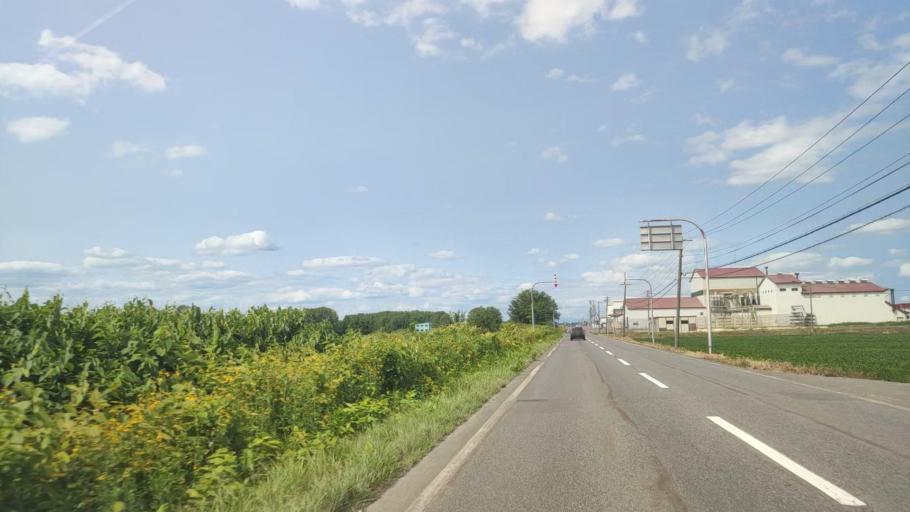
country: JP
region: Hokkaido
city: Nayoro
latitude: 44.2020
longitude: 142.4158
